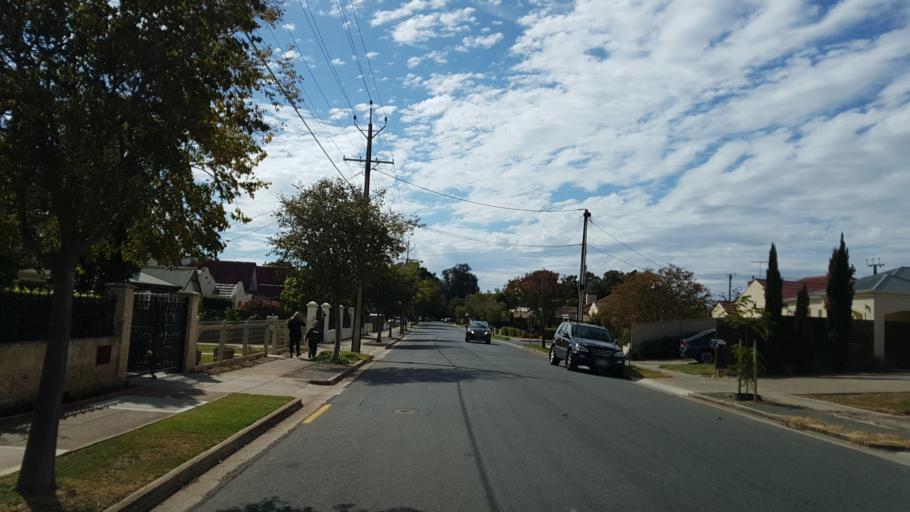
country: AU
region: South Australia
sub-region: City of West Torrens
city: Thebarton
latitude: -34.9280
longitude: 138.5497
